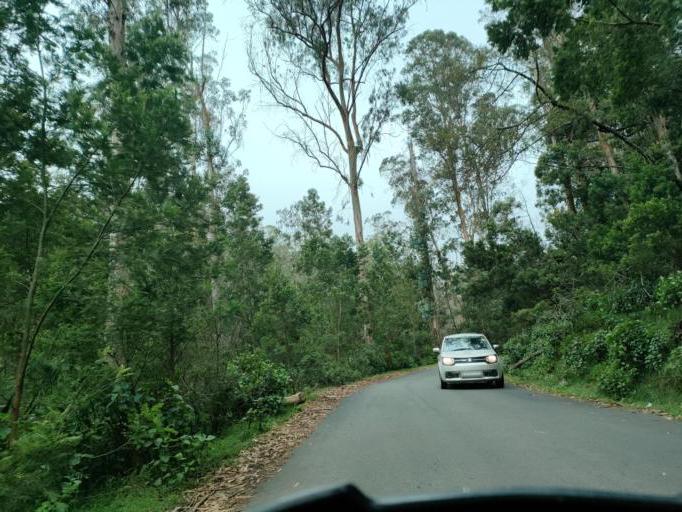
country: IN
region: Tamil Nadu
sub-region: Dindigul
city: Kodaikanal
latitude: 10.2421
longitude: 77.3712
